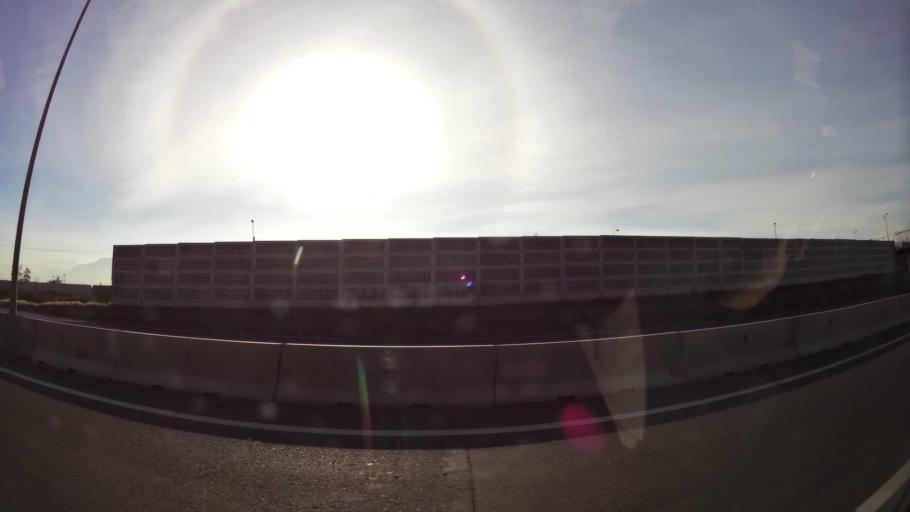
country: CL
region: Santiago Metropolitan
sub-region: Provincia de Santiago
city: La Pintana
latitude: -33.5802
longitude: -70.6113
